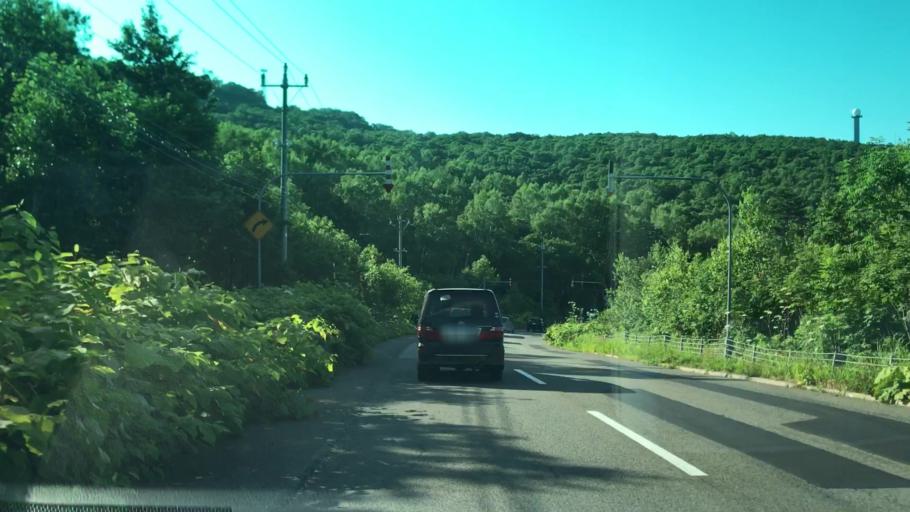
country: JP
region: Hokkaido
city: Otaru
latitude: 43.1313
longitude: 141.0123
